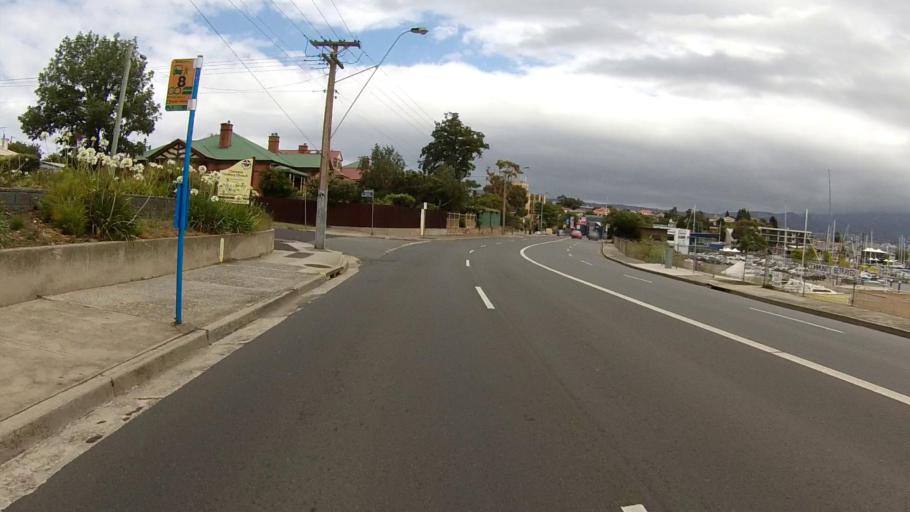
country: AU
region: Tasmania
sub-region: Clarence
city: Bellerive
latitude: -42.8728
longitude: 147.3695
